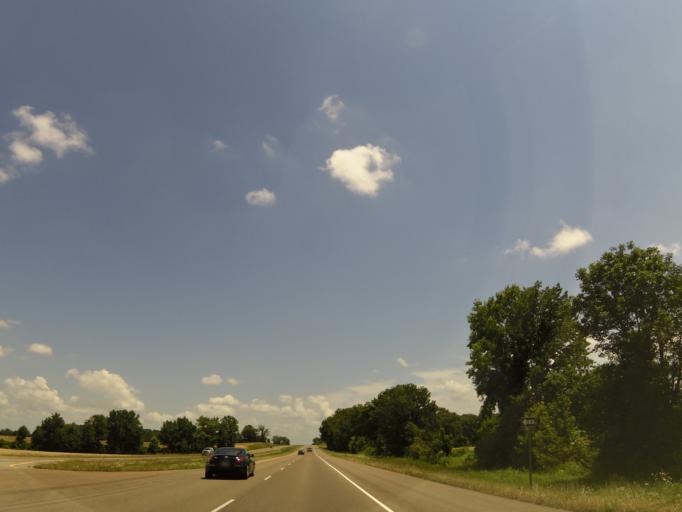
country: US
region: Tennessee
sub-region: Crockett County
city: Alamo
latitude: 35.8762
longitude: -89.2212
